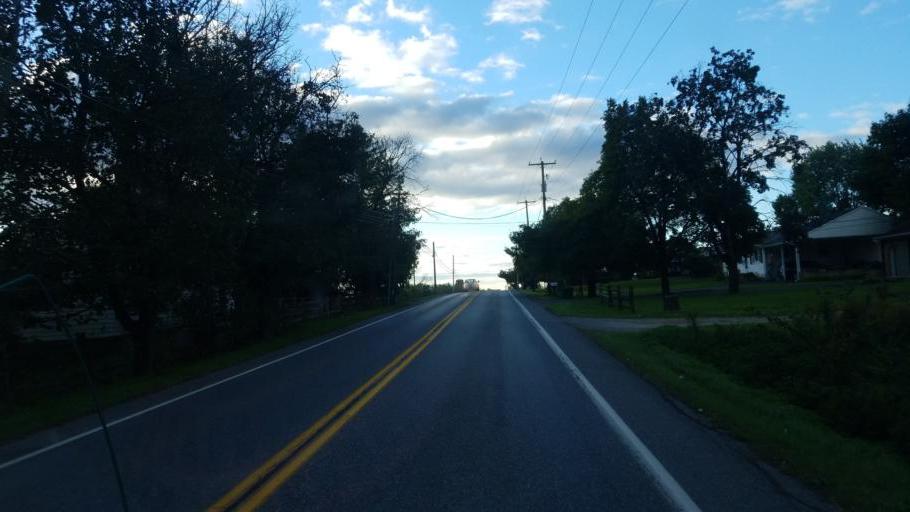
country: US
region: Pennsylvania
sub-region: Adams County
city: Lake Meade
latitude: 39.9364
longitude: -77.0616
